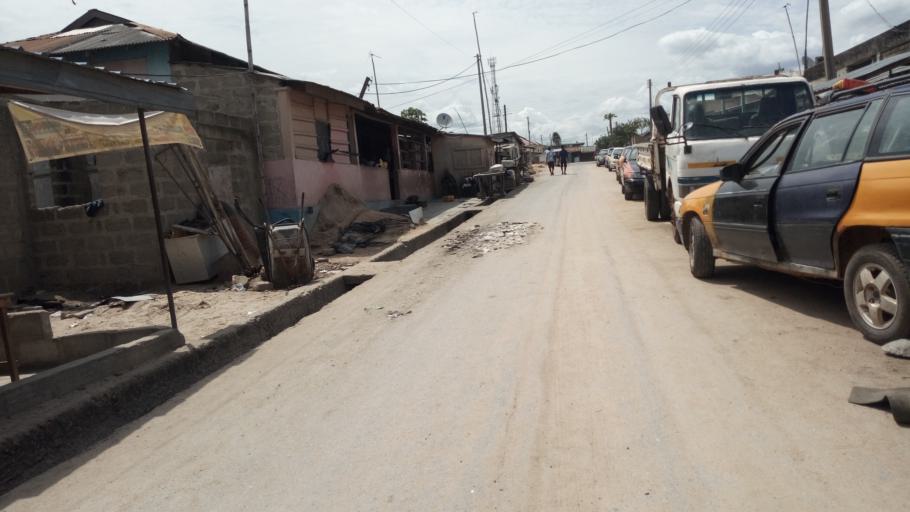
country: GH
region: Central
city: Winneba
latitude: 5.3466
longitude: -0.6202
